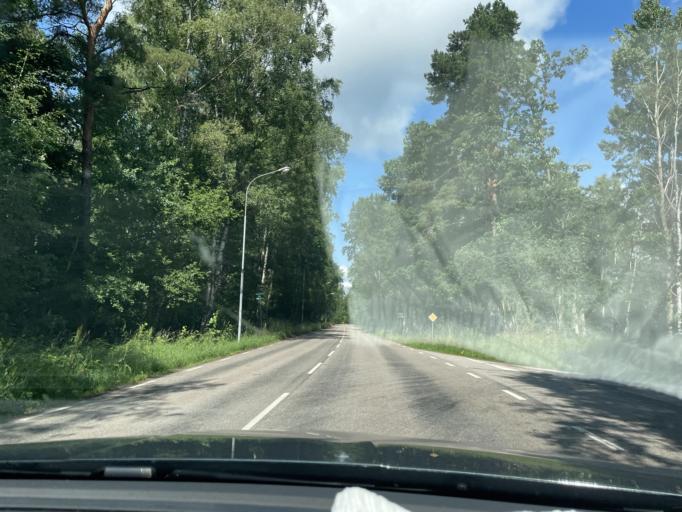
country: SE
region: Kronoberg
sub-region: Vaxjo Kommun
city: Vaexjoe
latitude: 56.8499
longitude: 14.8565
